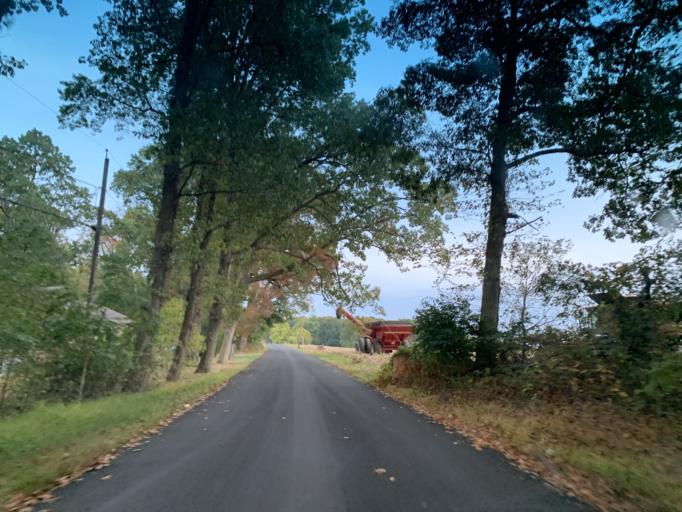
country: US
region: Pennsylvania
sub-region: York County
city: Stewartstown
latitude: 39.6765
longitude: -76.6350
